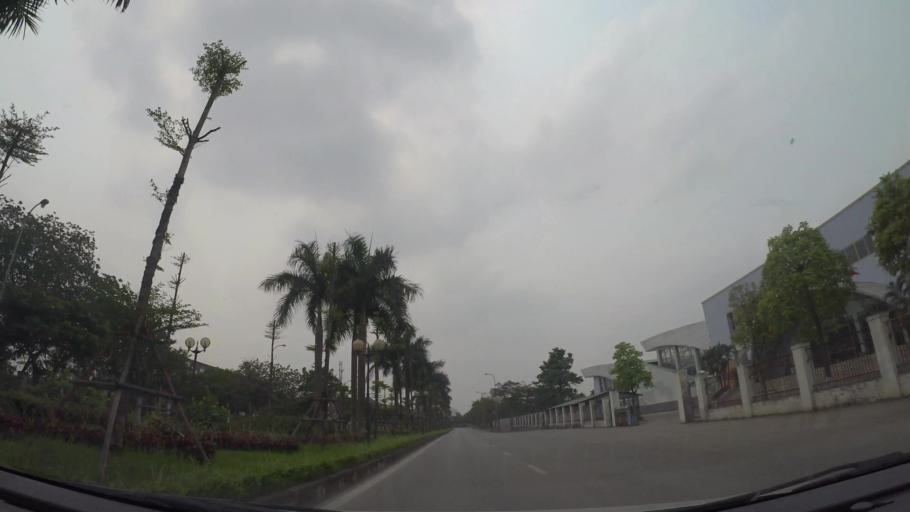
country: VN
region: Ha Noi
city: Cau Dien
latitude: 21.0256
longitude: 105.7616
